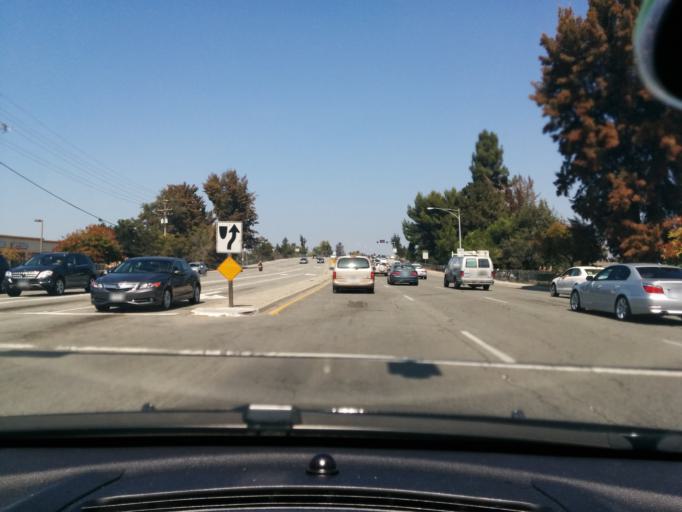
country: US
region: California
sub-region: Santa Clara County
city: Sunnyvale
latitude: 37.3668
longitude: -121.9961
